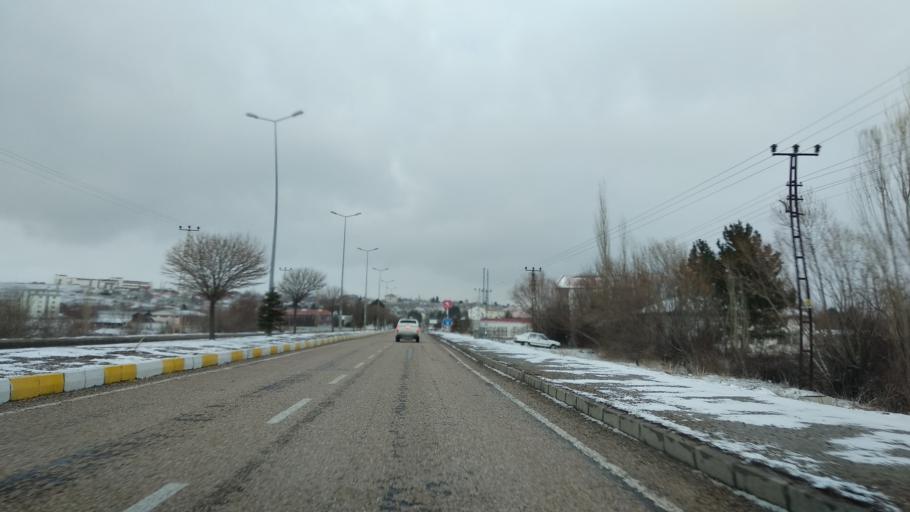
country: TR
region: Kayseri
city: Pinarbasi
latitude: 38.7168
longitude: 36.3830
